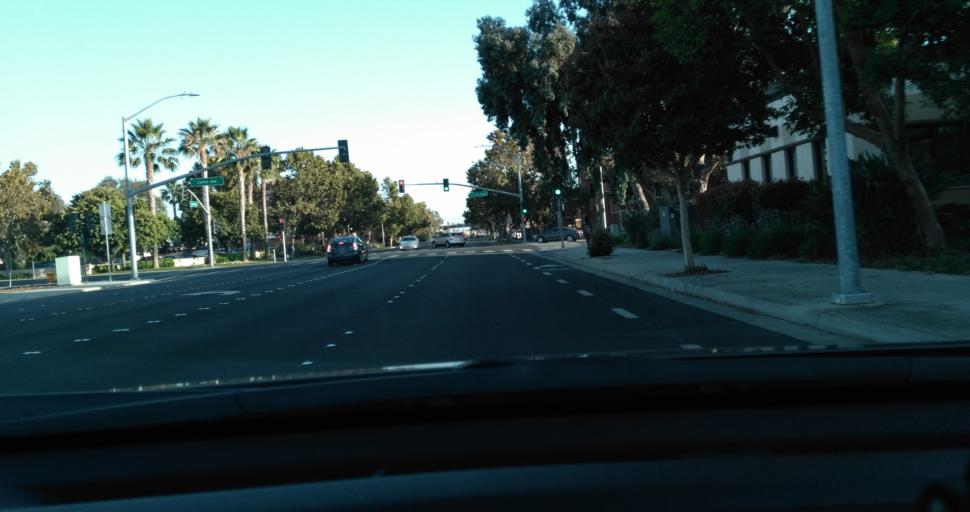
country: US
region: California
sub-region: Santa Clara County
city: Milpitas
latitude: 37.4194
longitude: -121.9040
